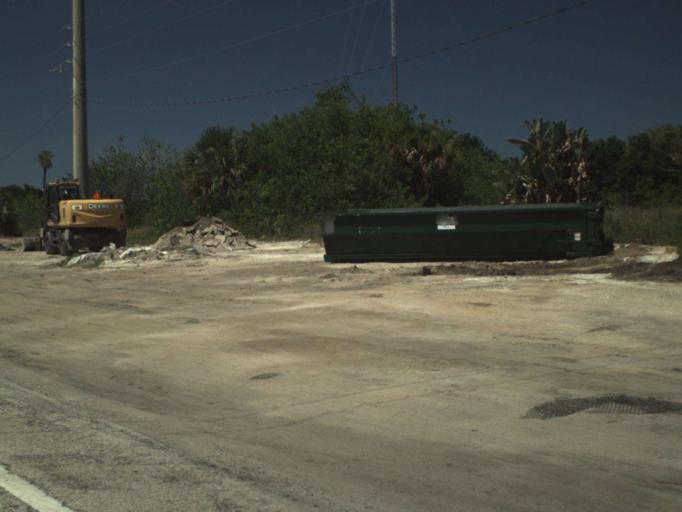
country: US
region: Florida
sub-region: Indian River County
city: Florida Ridge
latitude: 27.5537
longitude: -80.3698
